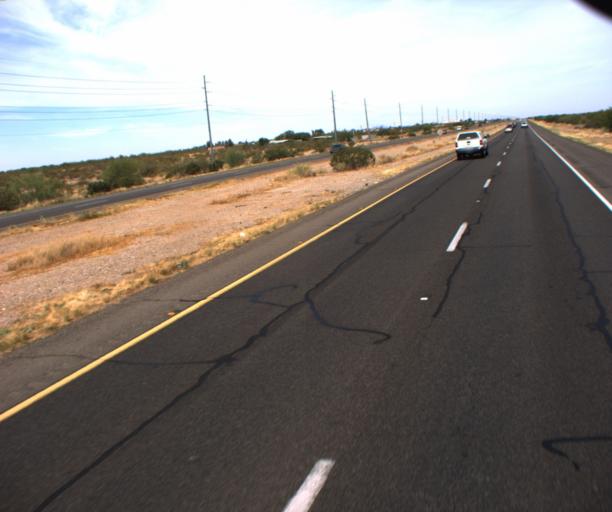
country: US
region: Arizona
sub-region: Maricopa County
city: Sun City West
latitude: 33.7006
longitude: -112.4294
